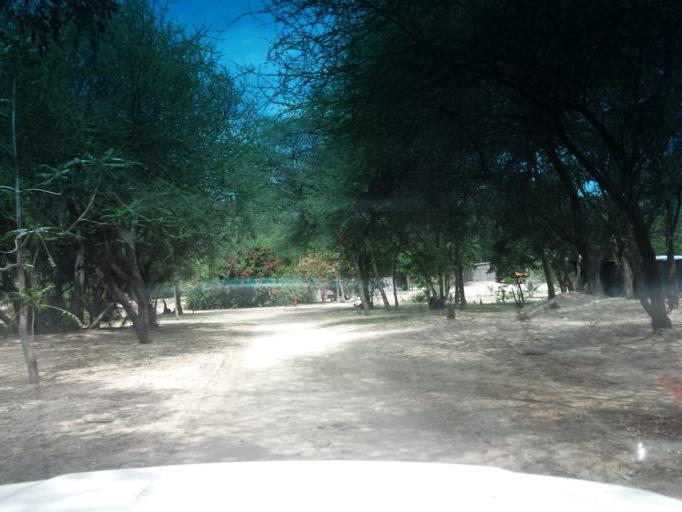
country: BW
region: North West
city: Shakawe
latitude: -18.7459
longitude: 22.1961
